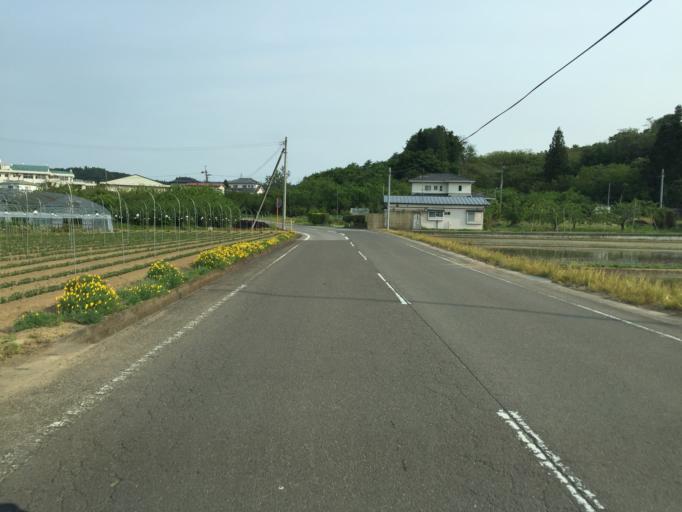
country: JP
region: Fukushima
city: Fukushima-shi
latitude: 37.7125
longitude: 140.4286
